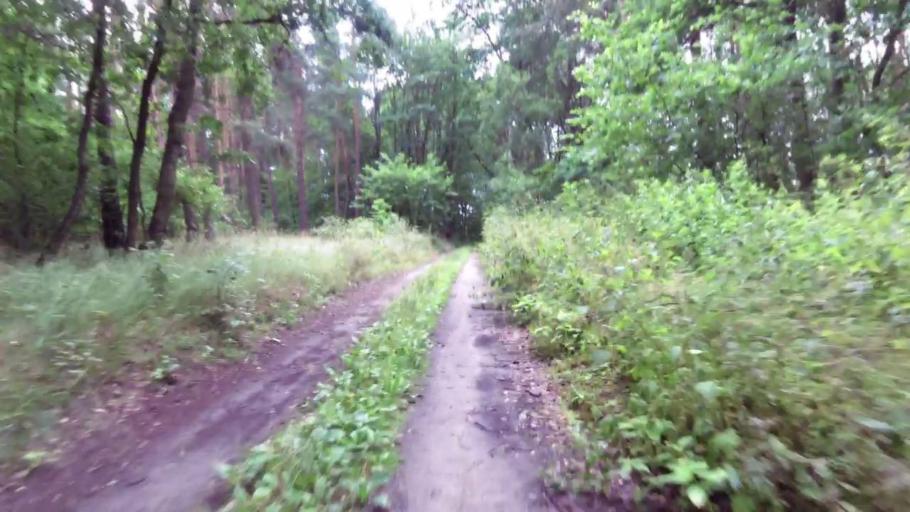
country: PL
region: West Pomeranian Voivodeship
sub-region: Powiat mysliborski
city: Mysliborz
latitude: 52.9641
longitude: 14.9133
